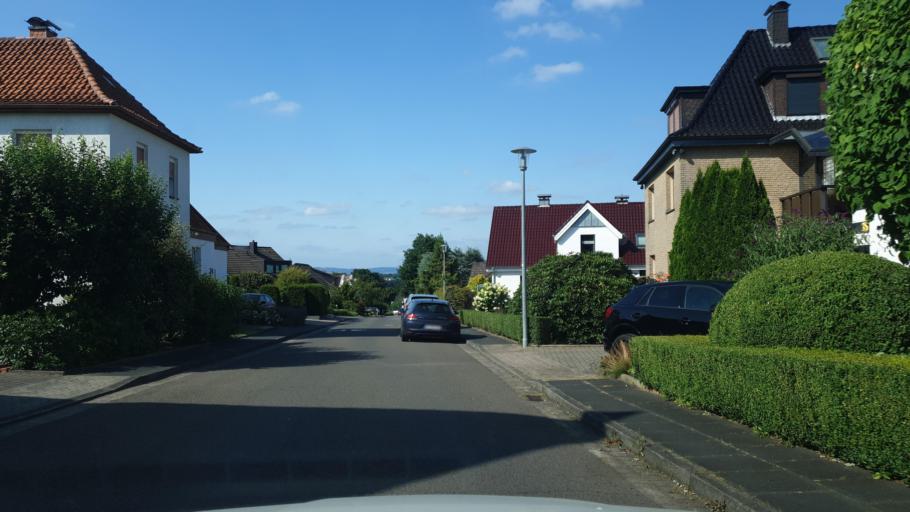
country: DE
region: North Rhine-Westphalia
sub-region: Regierungsbezirk Detmold
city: Hiddenhausen
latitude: 52.1310
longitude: 8.6238
